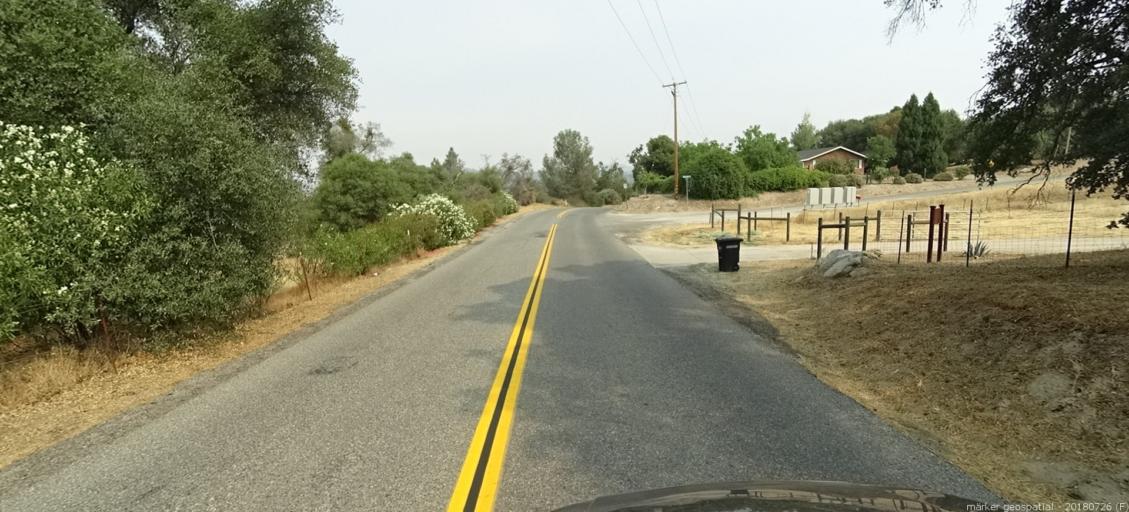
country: US
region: California
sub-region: Madera County
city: Coarsegold
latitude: 37.2151
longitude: -119.7009
